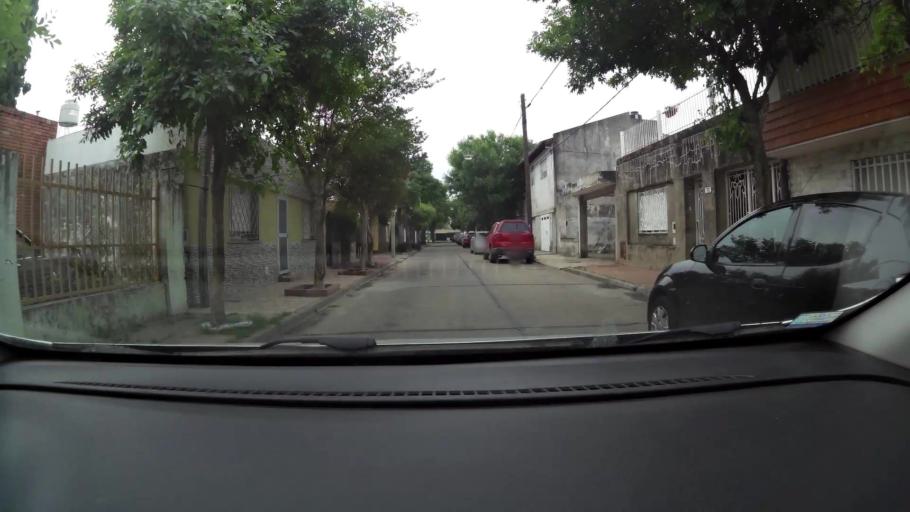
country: AR
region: Santa Fe
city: Granadero Baigorria
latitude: -32.9117
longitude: -60.6900
